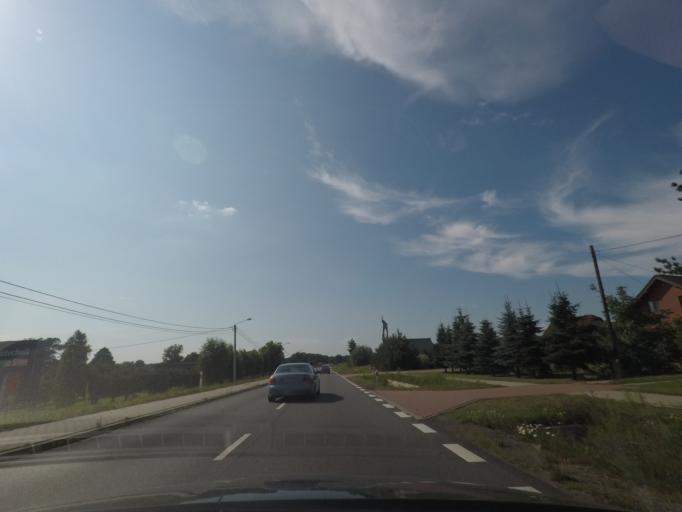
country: PL
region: Silesian Voivodeship
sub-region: Powiat pszczynski
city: Radostowice
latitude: 50.0111
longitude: 18.8607
